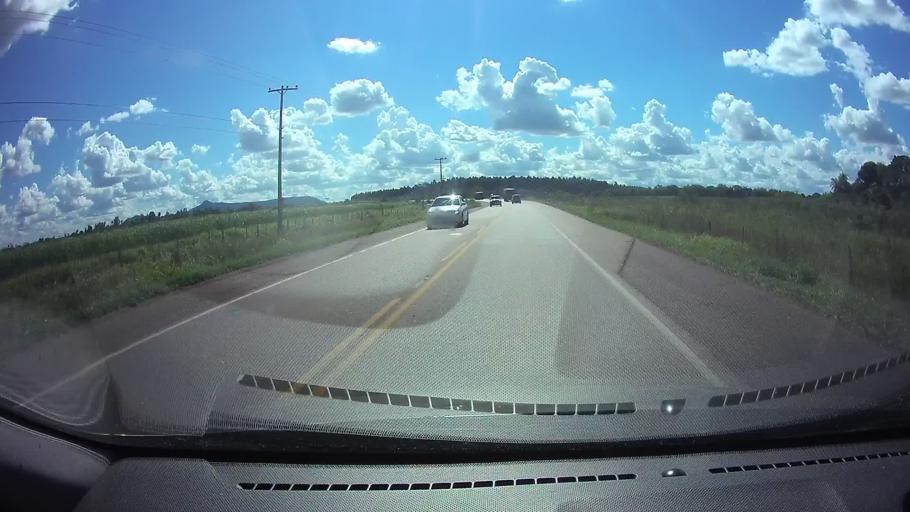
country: PY
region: Guaira
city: Coronel Martinez
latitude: -25.7589
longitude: -56.7027
